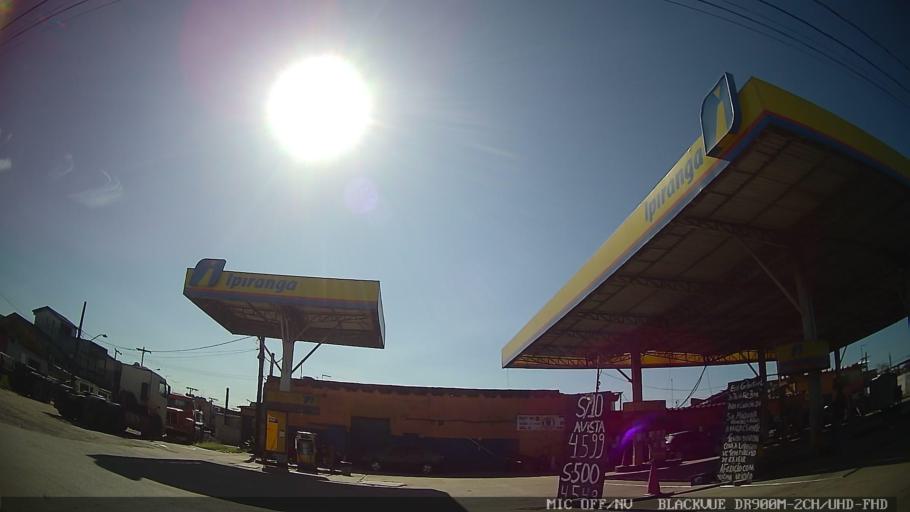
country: BR
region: Sao Paulo
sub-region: Guaruja
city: Guaruja
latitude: -23.9624
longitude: -46.2752
